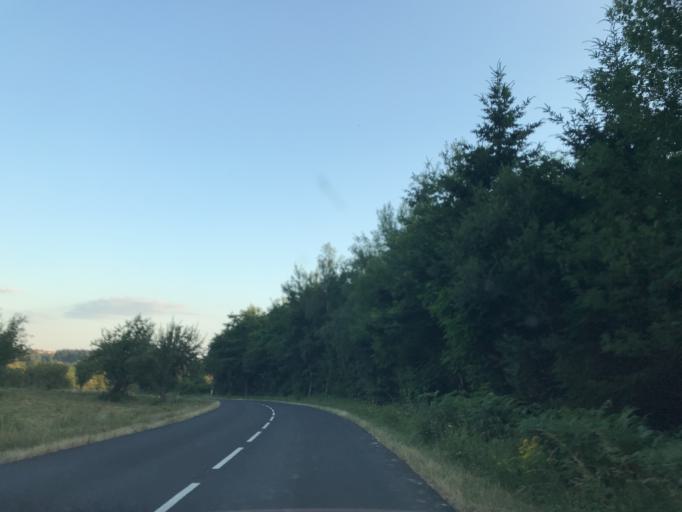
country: FR
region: Auvergne
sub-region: Departement du Puy-de-Dome
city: Courpiere
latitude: 45.7506
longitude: 3.6038
